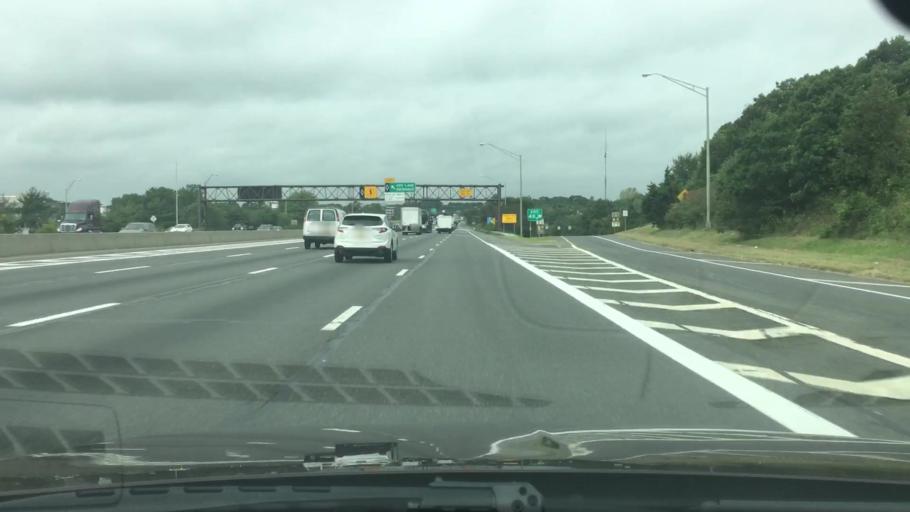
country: US
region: New York
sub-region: Nassau County
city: Old Bethpage
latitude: 40.7844
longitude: -73.4403
